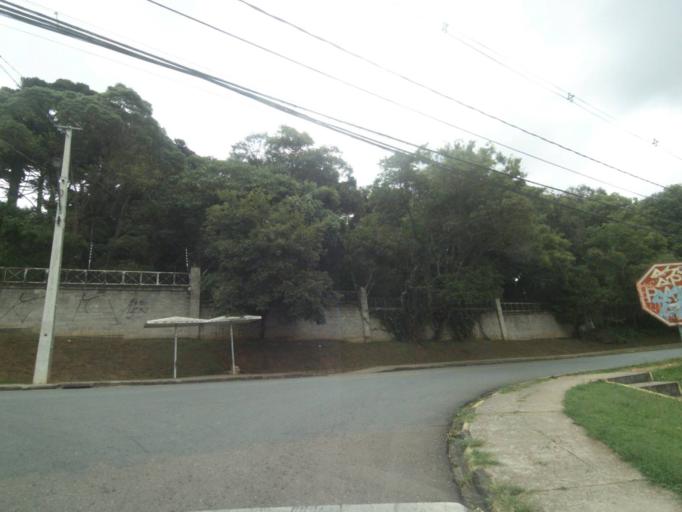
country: BR
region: Parana
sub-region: Curitiba
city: Curitiba
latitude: -25.3885
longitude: -49.2893
